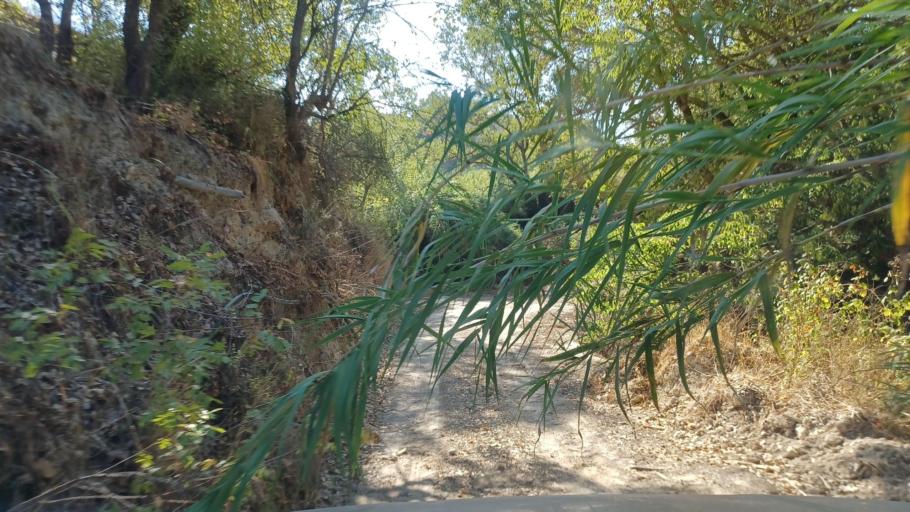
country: CY
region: Pafos
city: Tala
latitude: 34.9176
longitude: 32.4588
